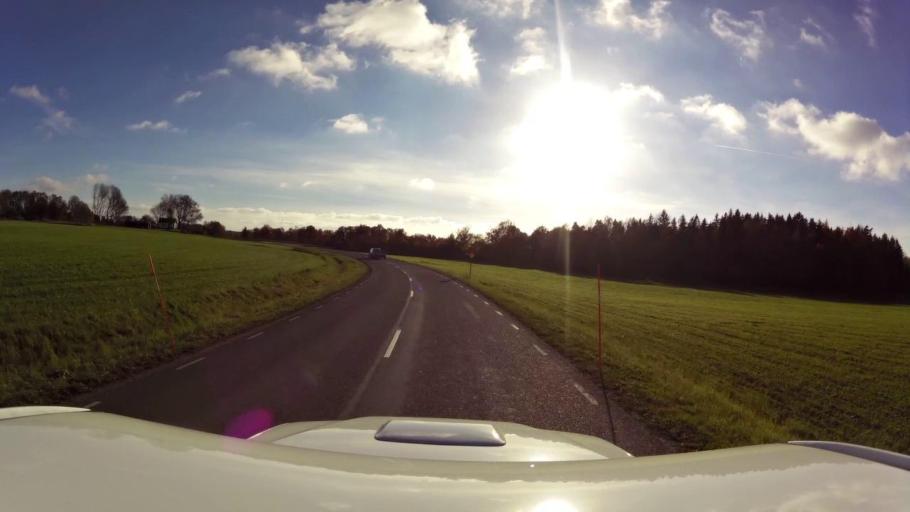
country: SE
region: OEstergoetland
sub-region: Linkopings Kommun
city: Malmslatt
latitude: 58.3366
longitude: 15.5127
